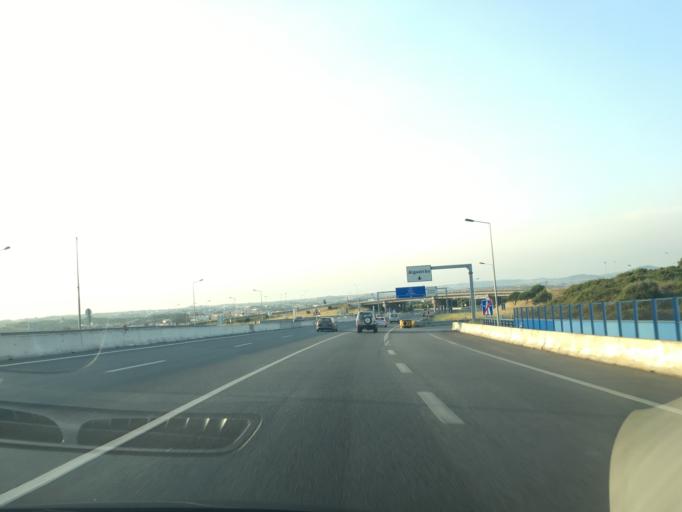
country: PT
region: Lisbon
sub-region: Sintra
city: Sintra
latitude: 38.8011
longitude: -9.3633
